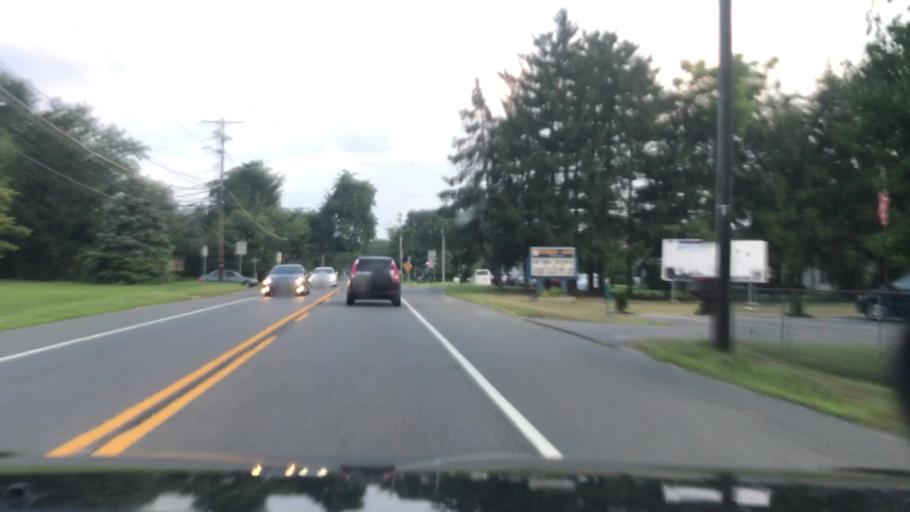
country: US
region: New Jersey
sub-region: Ocean County
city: Silver Ridge
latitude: 39.9815
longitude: -74.2097
